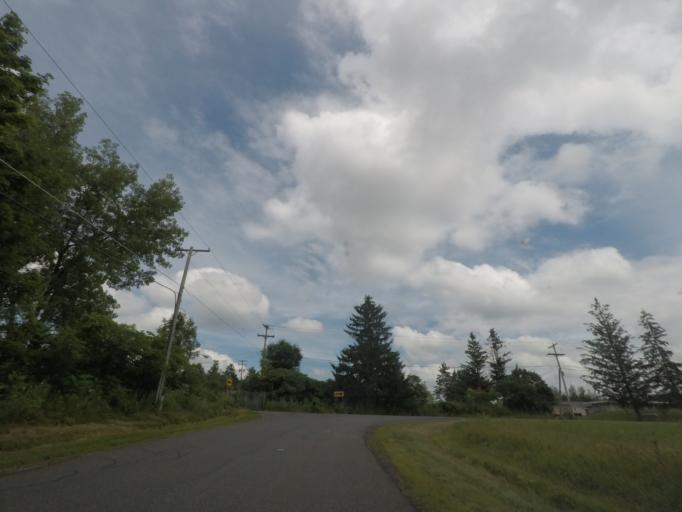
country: US
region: New York
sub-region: Saratoga County
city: Stillwater
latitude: 43.0092
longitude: -73.6865
